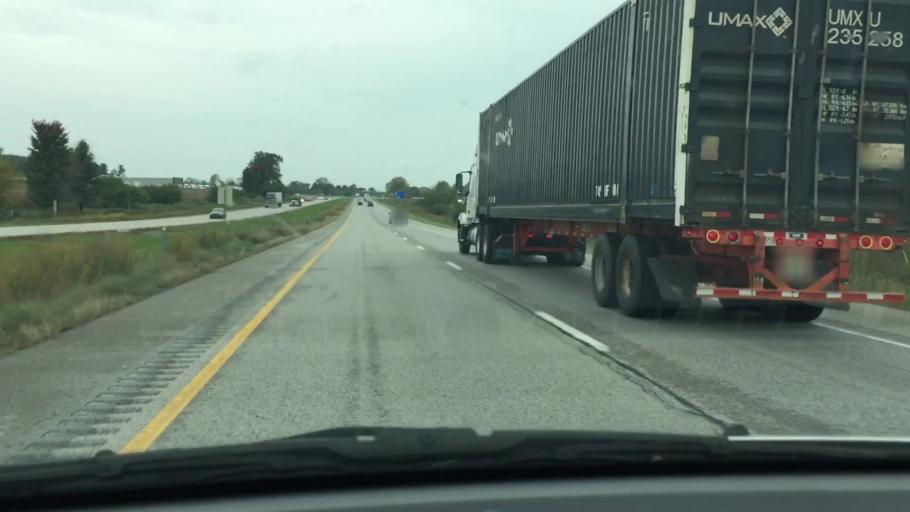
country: US
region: Iowa
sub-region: Johnson County
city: Tiffin
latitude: 41.6943
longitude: -91.6509
